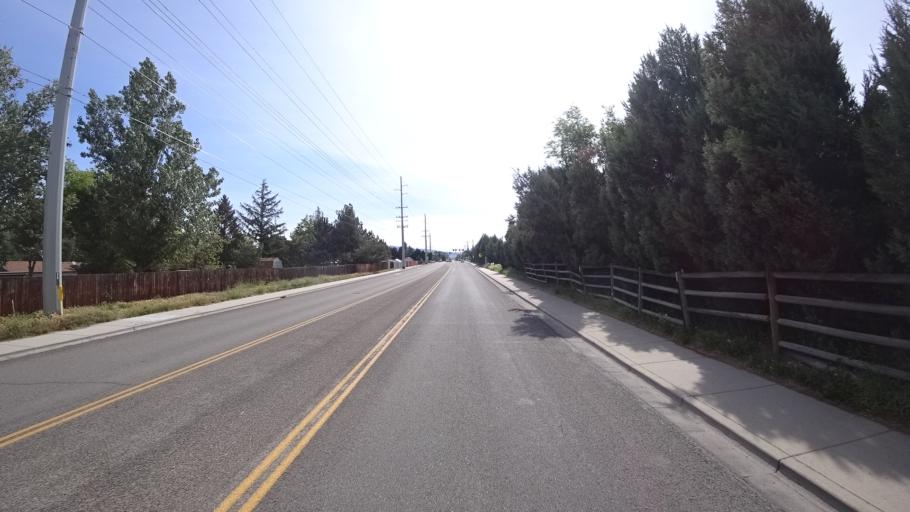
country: US
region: Idaho
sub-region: Ada County
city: Garden City
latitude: 43.5757
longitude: -116.2977
